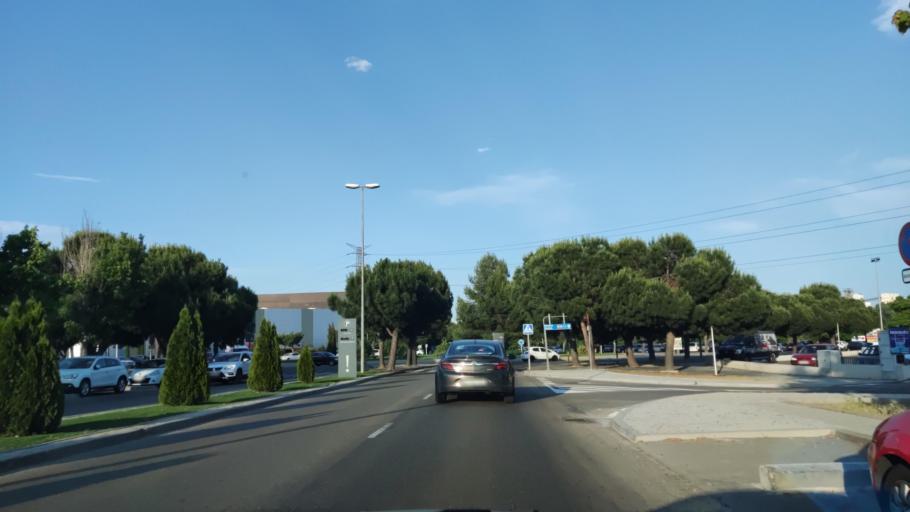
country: ES
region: Madrid
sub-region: Provincia de Madrid
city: Pinto
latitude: 40.2710
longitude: -3.6958
